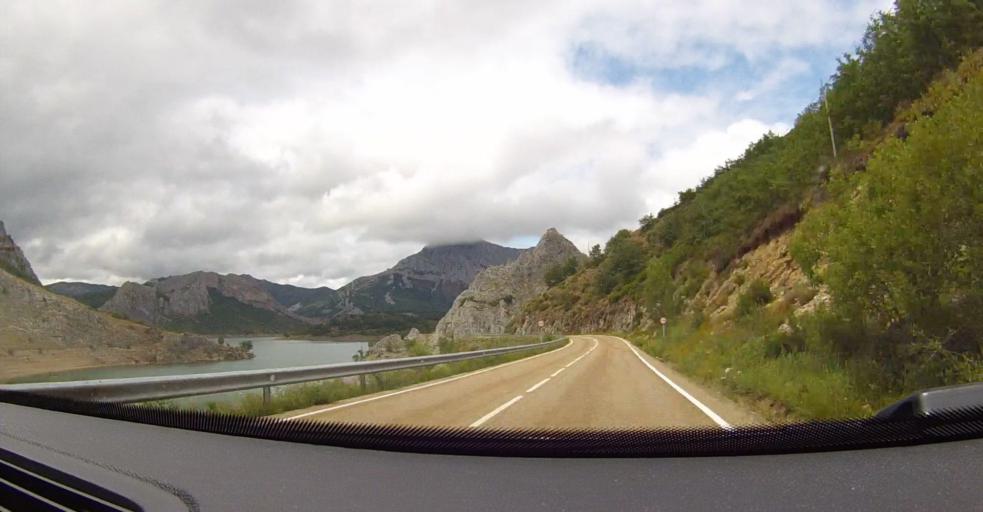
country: ES
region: Castille and Leon
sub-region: Provincia de Leon
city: Reyero
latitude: 42.9566
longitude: -5.2502
